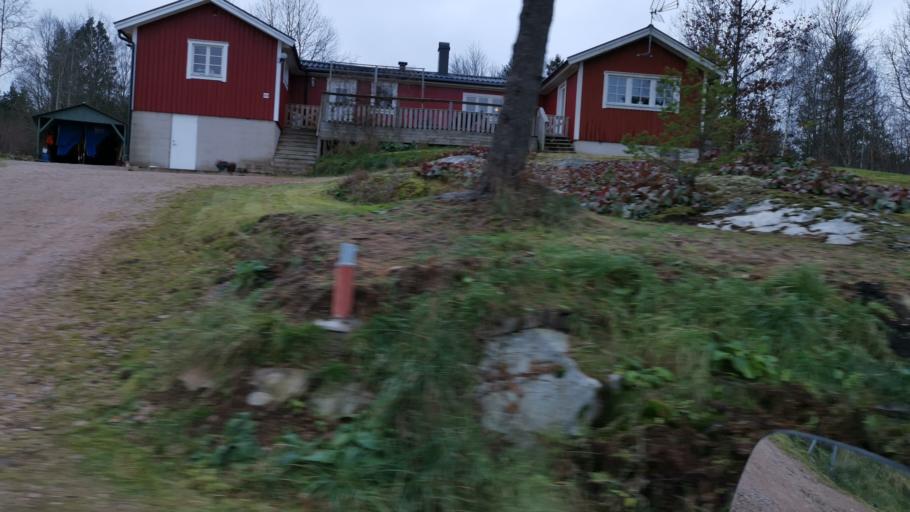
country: SE
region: Vaestra Goetaland
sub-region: Orust
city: Henan
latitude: 58.2239
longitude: 11.7039
